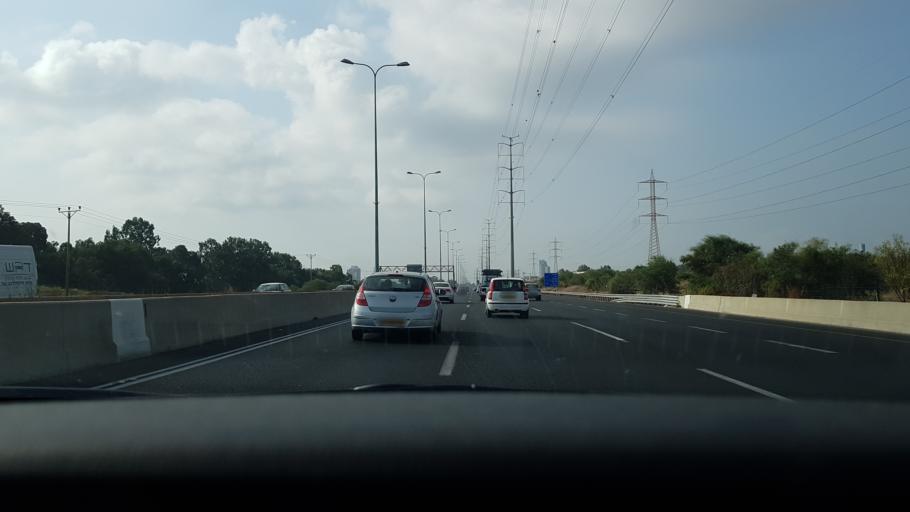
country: IL
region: Central District
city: Bet Dagan
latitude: 31.9939
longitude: 34.7992
